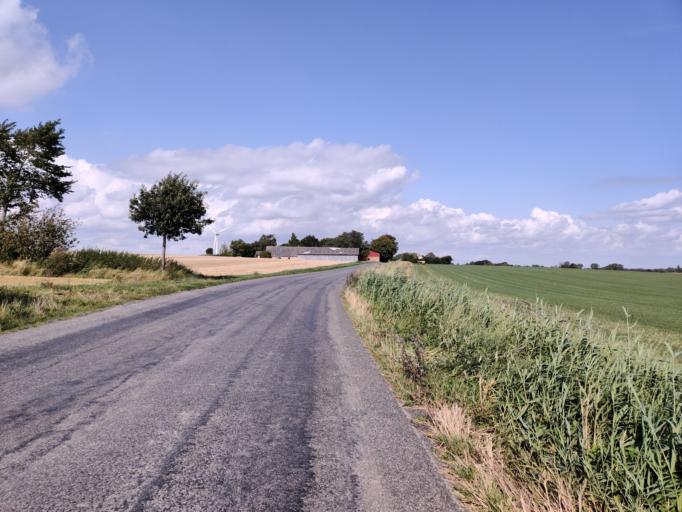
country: DK
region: Zealand
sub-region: Guldborgsund Kommune
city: Nykobing Falster
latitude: 54.6560
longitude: 11.8878
